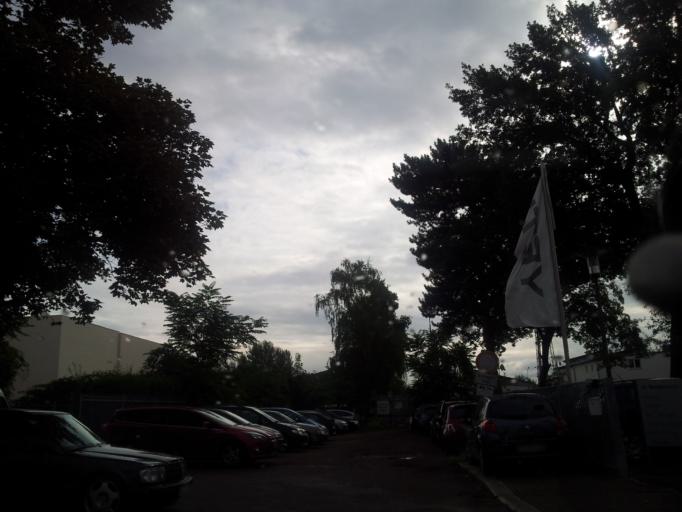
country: DE
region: Saxony-Anhalt
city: Halle (Saale)
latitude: 51.4707
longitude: 11.9844
